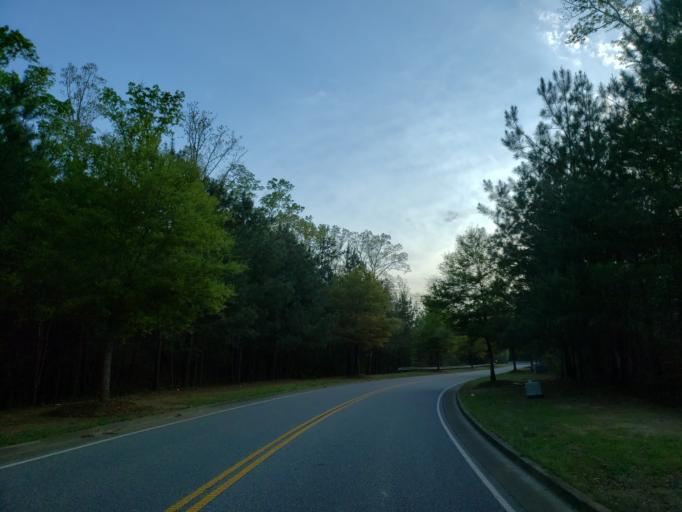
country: US
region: Georgia
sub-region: Cherokee County
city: Canton
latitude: 34.2886
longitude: -84.4638
